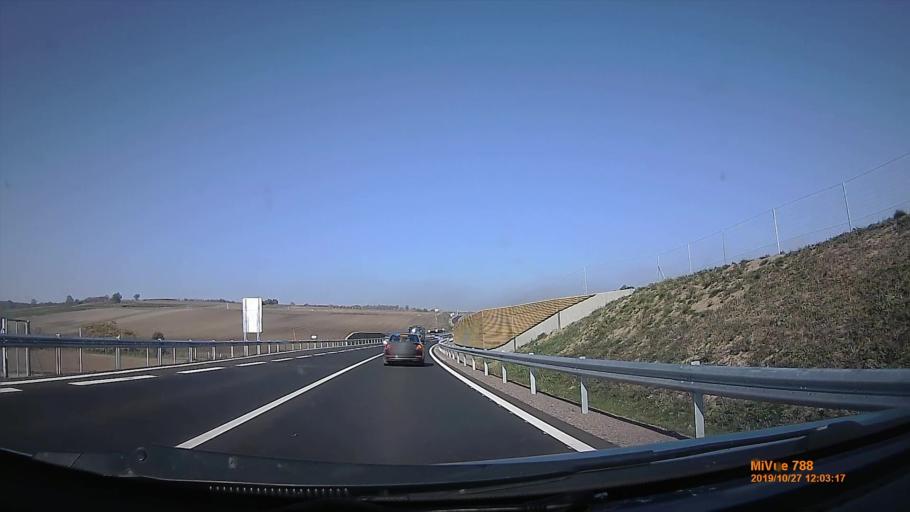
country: AT
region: Lower Austria
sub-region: Politischer Bezirk Mistelbach
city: Drasenhofen
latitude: 48.7411
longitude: 16.6386
